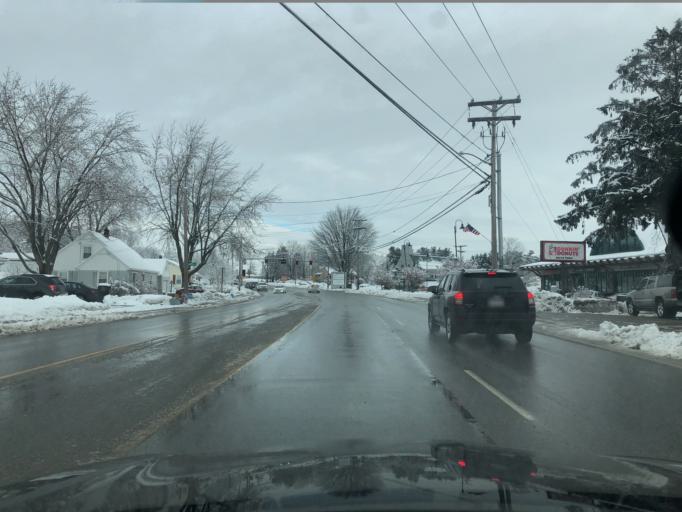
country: US
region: New Hampshire
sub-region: Strafford County
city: Somersworth
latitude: 43.2387
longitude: -70.8794
